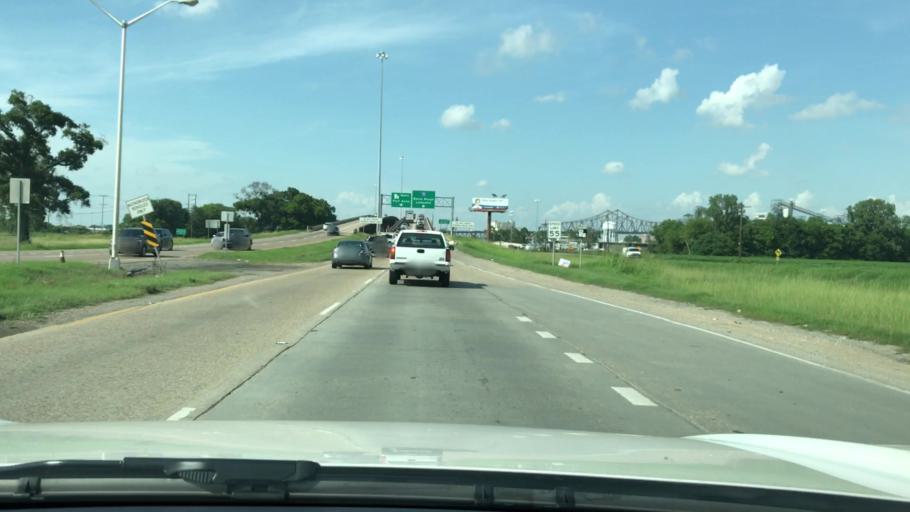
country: US
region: Louisiana
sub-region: West Baton Rouge Parish
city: Port Allen
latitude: 30.4279
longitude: -91.2141
